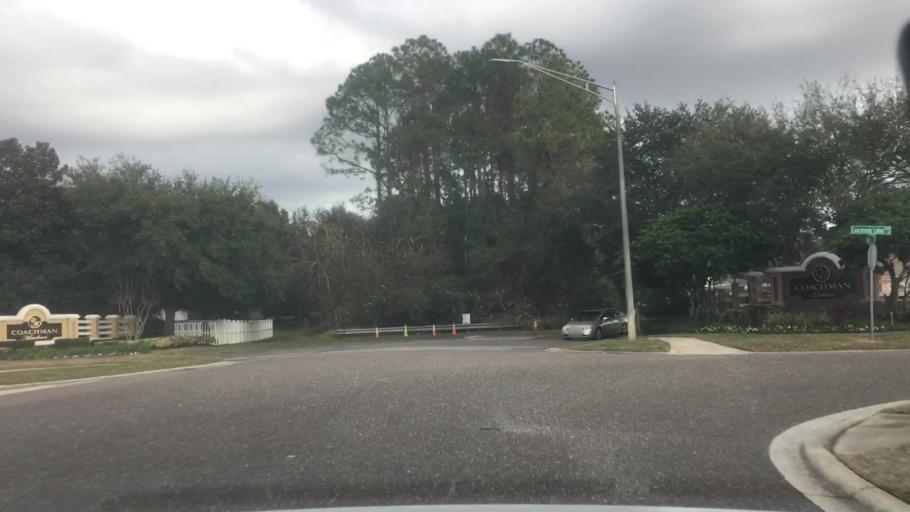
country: US
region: Florida
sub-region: Duval County
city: Neptune Beach
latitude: 30.3021
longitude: -81.5028
